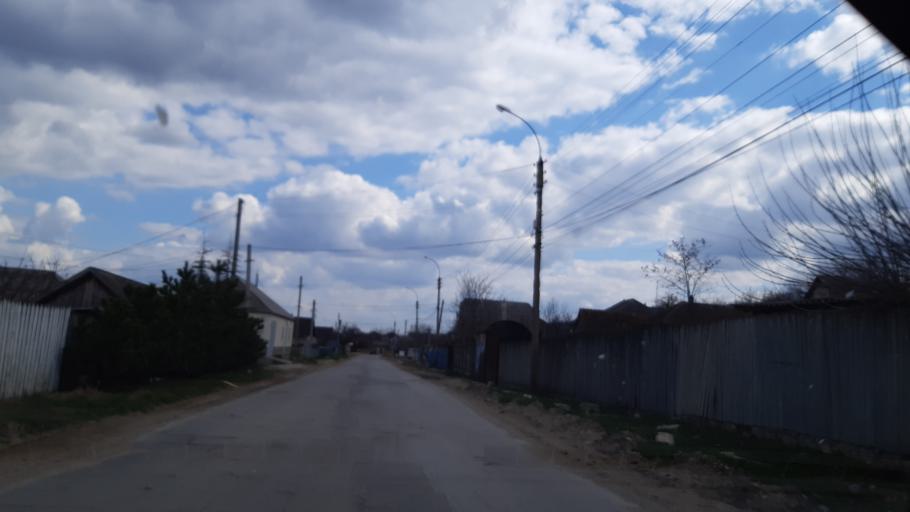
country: MD
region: Laloveni
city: Ialoveni
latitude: 46.8745
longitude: 28.7602
